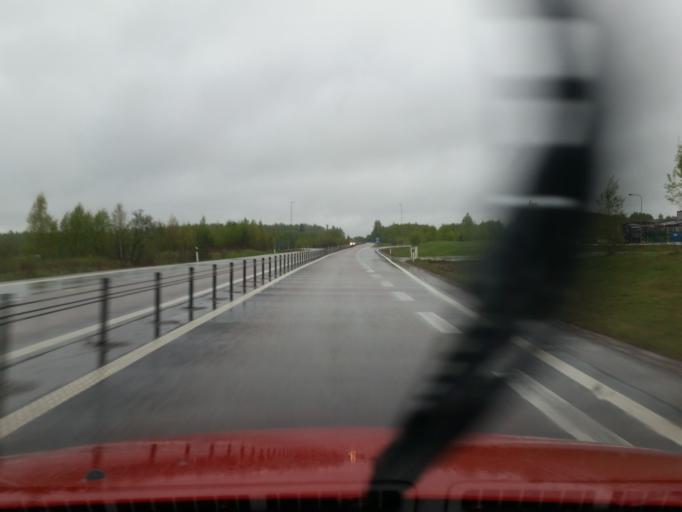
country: SE
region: Dalarna
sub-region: Borlange Kommun
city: Ornas
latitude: 60.4413
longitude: 15.5048
